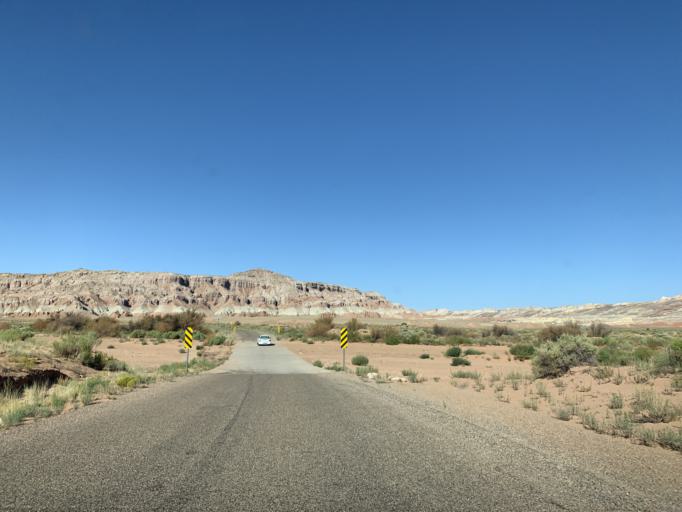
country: US
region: Utah
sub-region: Emery County
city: Ferron
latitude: 38.5762
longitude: -110.7450
